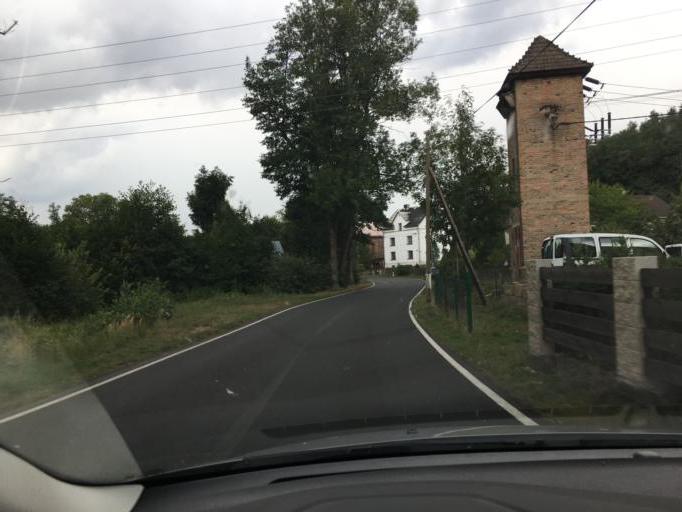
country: CZ
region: Ustecky
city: Ceska Kamenice
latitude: 50.8043
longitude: 14.3678
